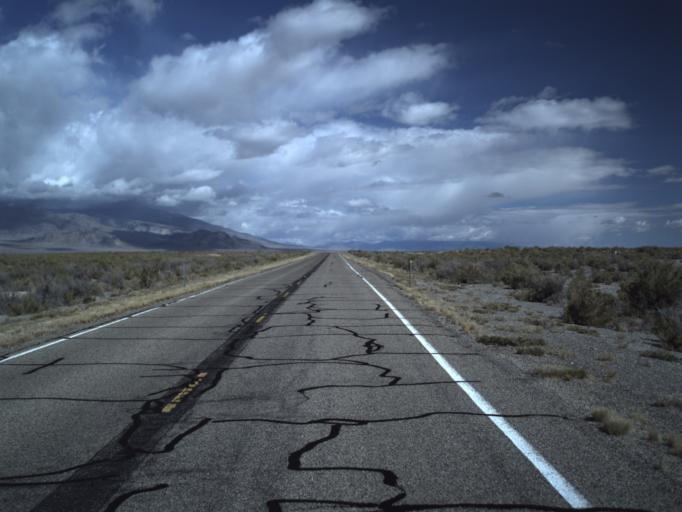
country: US
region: Nevada
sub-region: White Pine County
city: McGill
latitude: 39.0359
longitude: -114.0359
